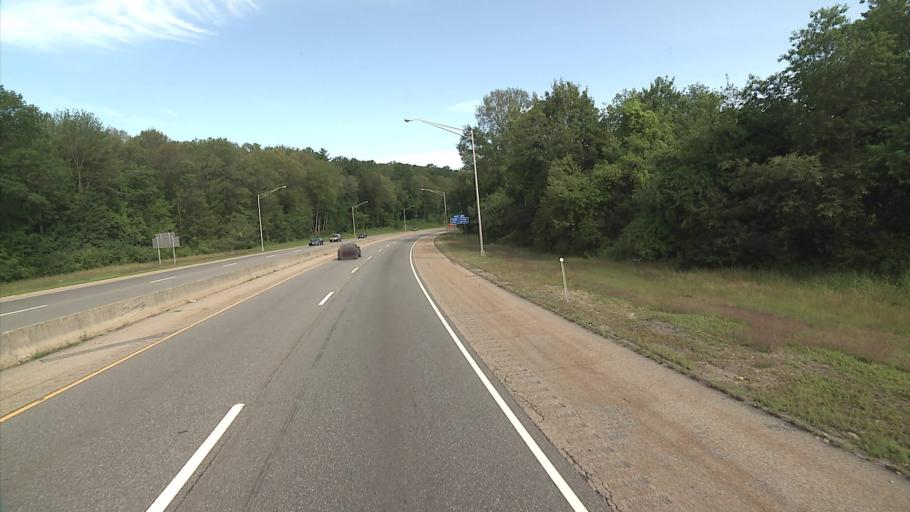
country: US
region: Connecticut
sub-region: New London County
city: Norwich
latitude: 41.5485
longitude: -72.1157
